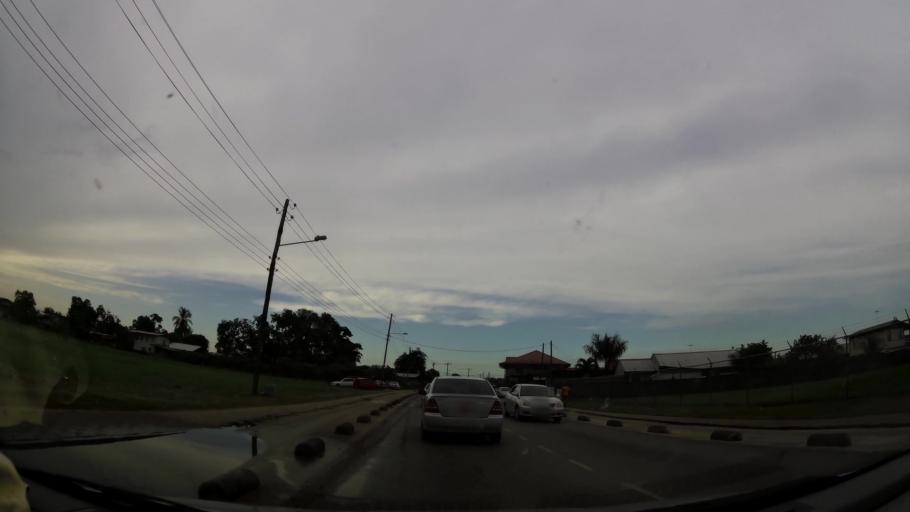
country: SR
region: Paramaribo
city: Paramaribo
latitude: 5.7968
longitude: -55.1896
